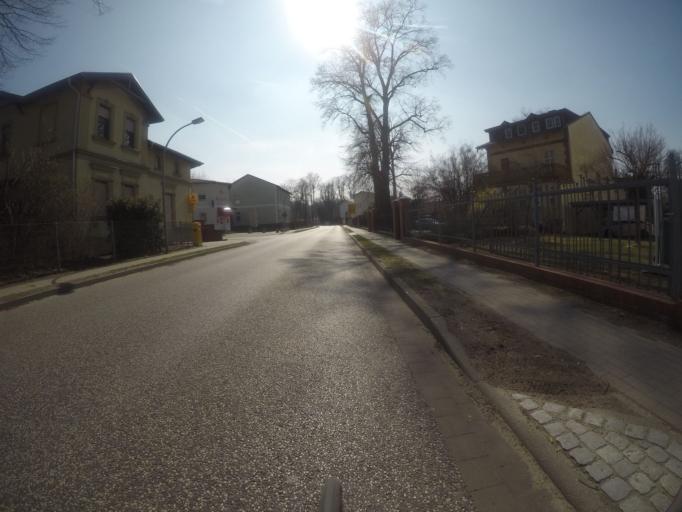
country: DE
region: Brandenburg
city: Konigs Wusterhausen
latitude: 52.2990
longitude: 13.6505
